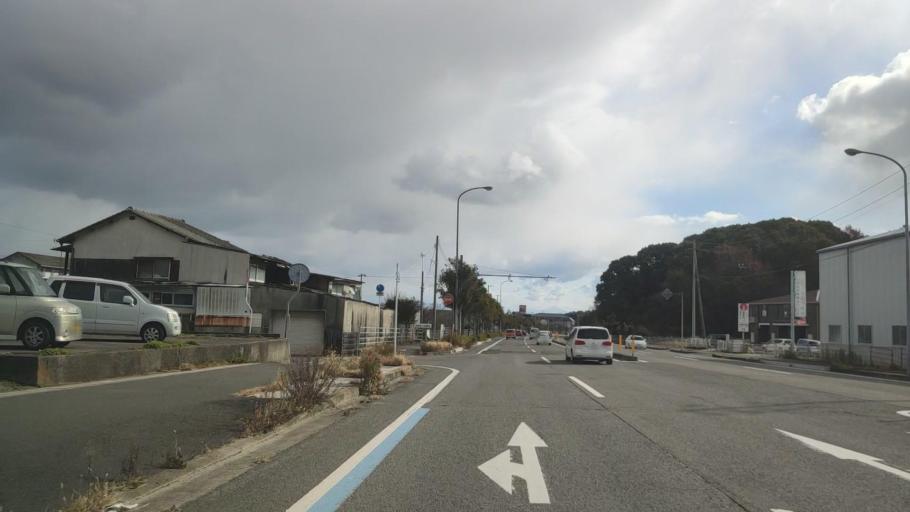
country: JP
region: Ehime
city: Hojo
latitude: 34.0619
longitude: 132.9607
